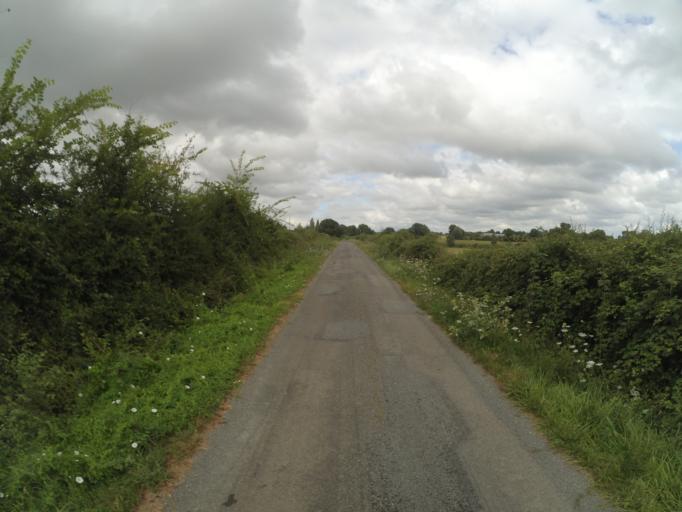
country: FR
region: Pays de la Loire
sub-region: Departement de la Vendee
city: Saint-Philbert-de-Bouaine
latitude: 46.9896
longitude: -1.4826
